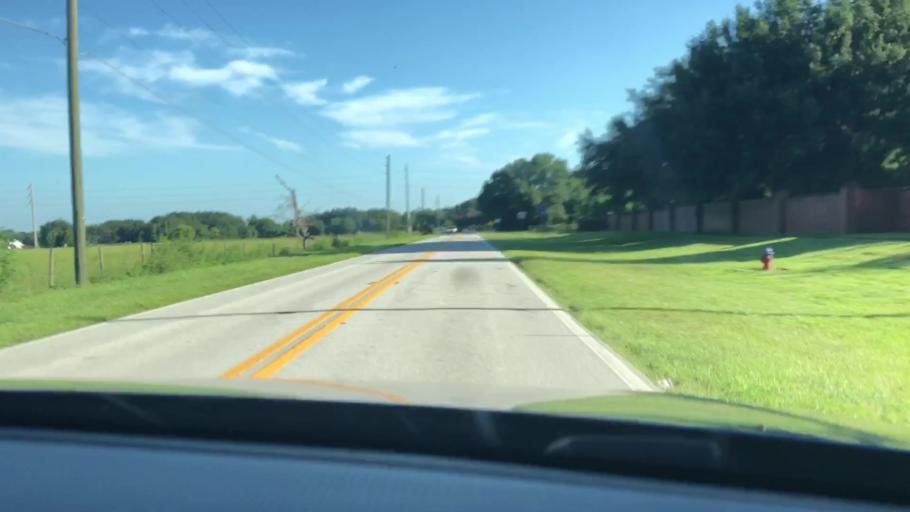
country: US
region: Florida
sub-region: Lake County
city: Eustis
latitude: 28.8663
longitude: -81.6530
